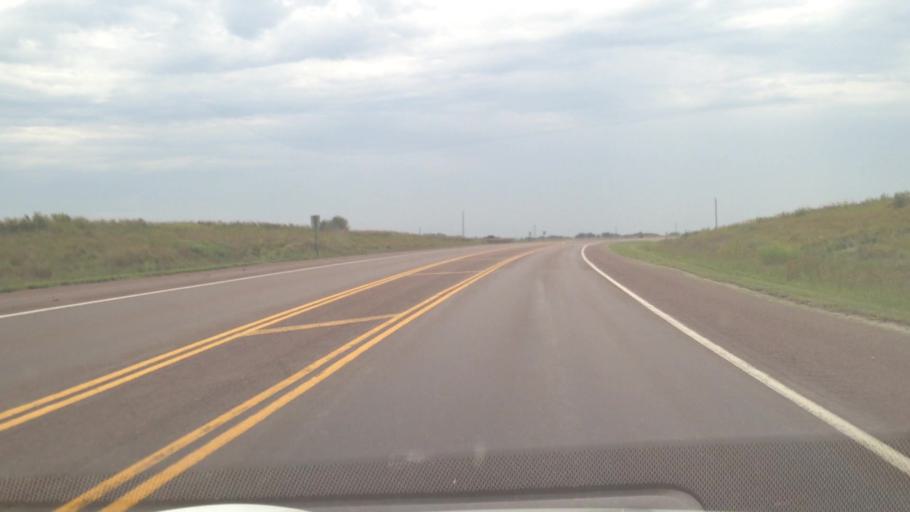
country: US
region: Kansas
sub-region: Crawford County
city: Girard
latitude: 37.4720
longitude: -94.8358
